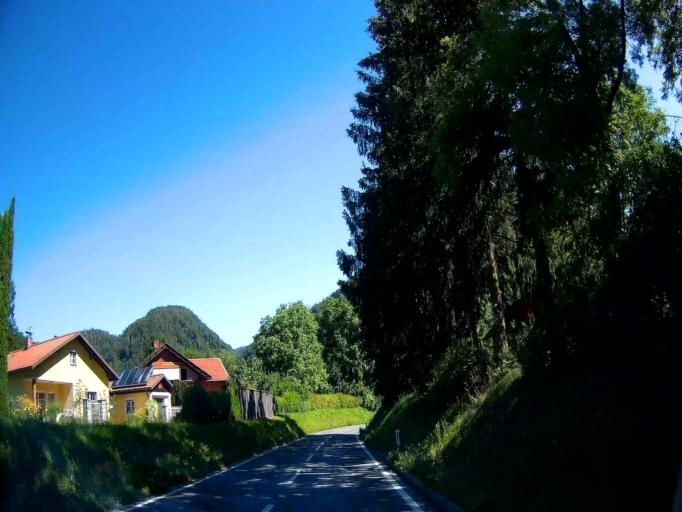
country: AT
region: Carinthia
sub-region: Politischer Bezirk Volkermarkt
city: Diex
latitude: 46.7005
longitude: 14.5830
